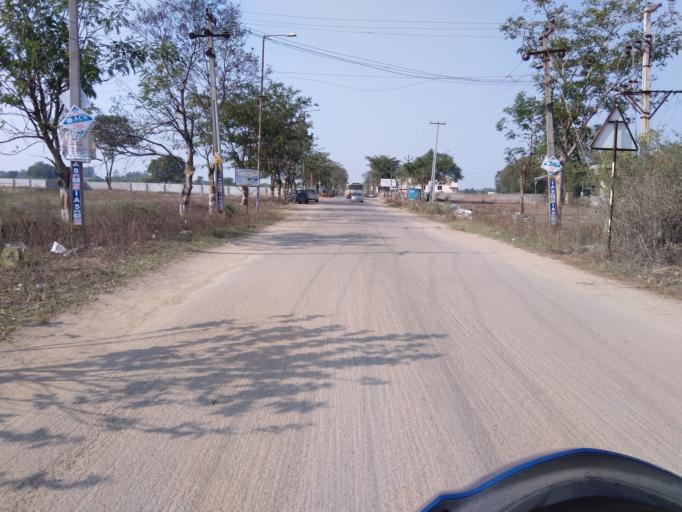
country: IN
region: Telangana
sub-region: Rangareddi
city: Quthbullapur
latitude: 17.5977
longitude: 78.4165
